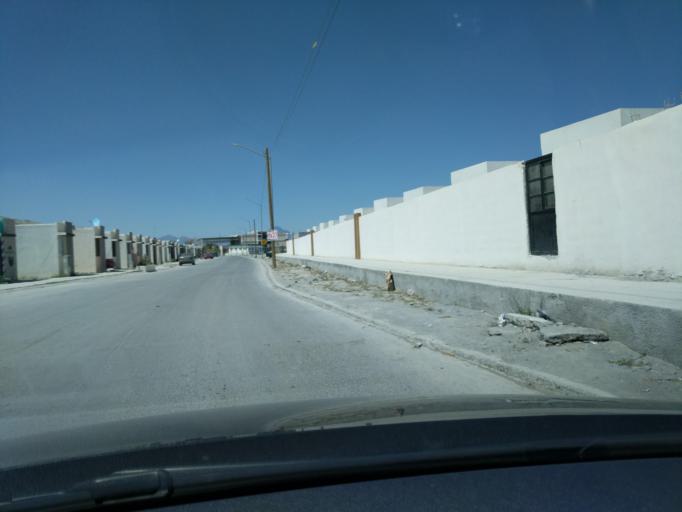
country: MX
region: Nuevo Leon
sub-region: Apodaca
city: Artemio Trevino
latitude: 25.8404
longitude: -100.1388
